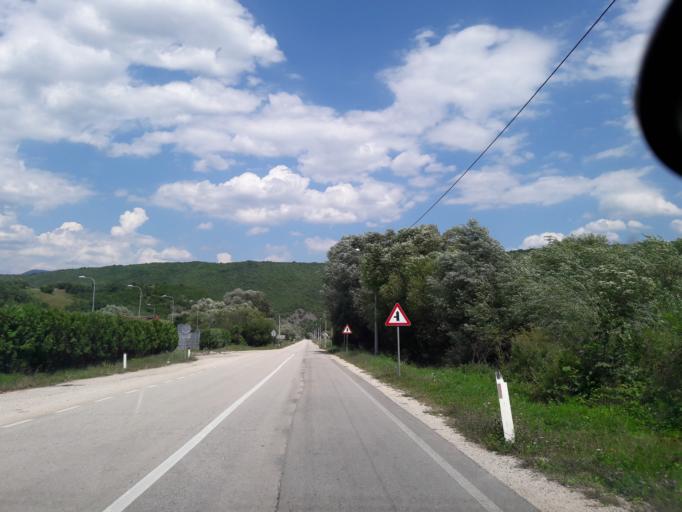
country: BA
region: Republika Srpska
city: Mrkonjic Grad
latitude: 44.4391
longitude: 17.1546
